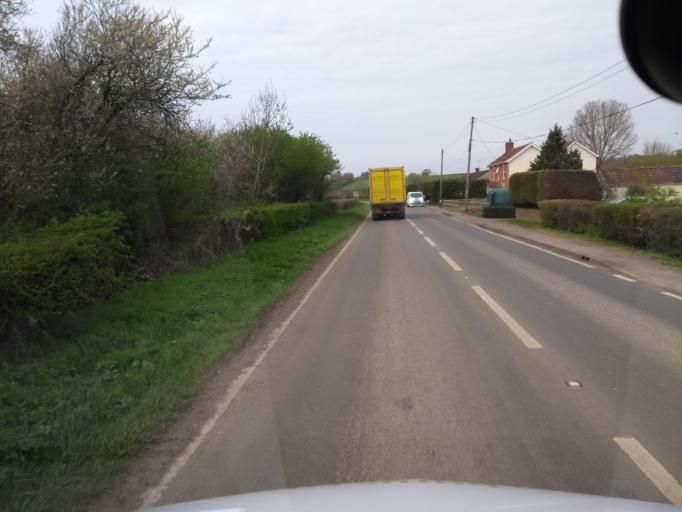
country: GB
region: England
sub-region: Somerset
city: Creech Saint Michael
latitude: 50.9970
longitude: -2.9936
